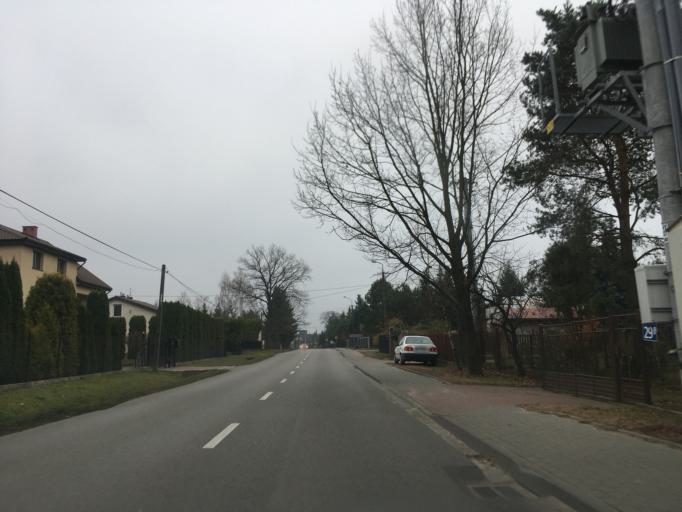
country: PL
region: Masovian Voivodeship
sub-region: Powiat piaseczynski
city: Lesznowola
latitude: 52.0515
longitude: 20.9290
